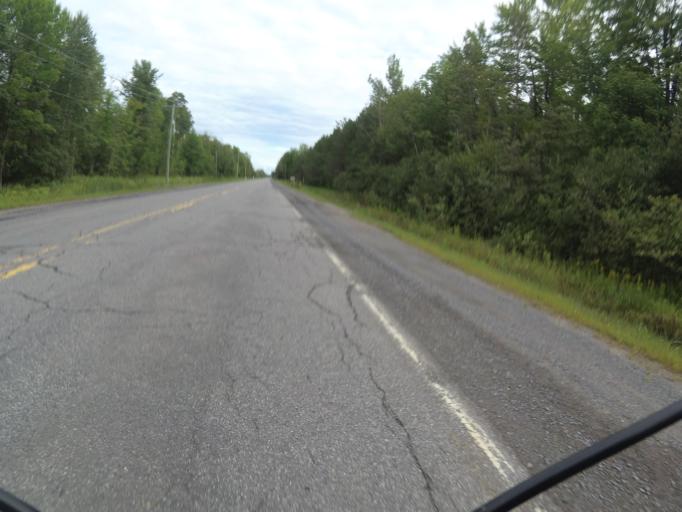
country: CA
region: Ontario
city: Bourget
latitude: 45.3603
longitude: -75.2616
